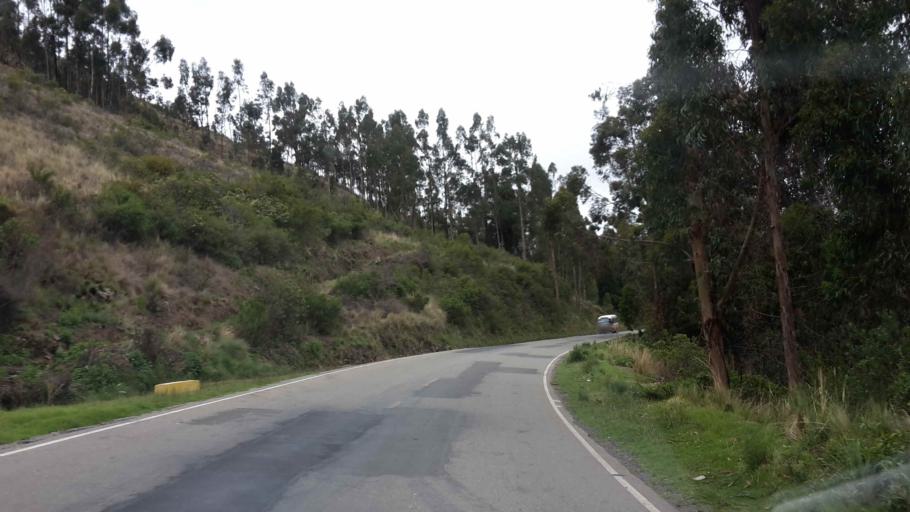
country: BO
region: Cochabamba
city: Arani
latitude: -17.4783
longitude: -65.5367
